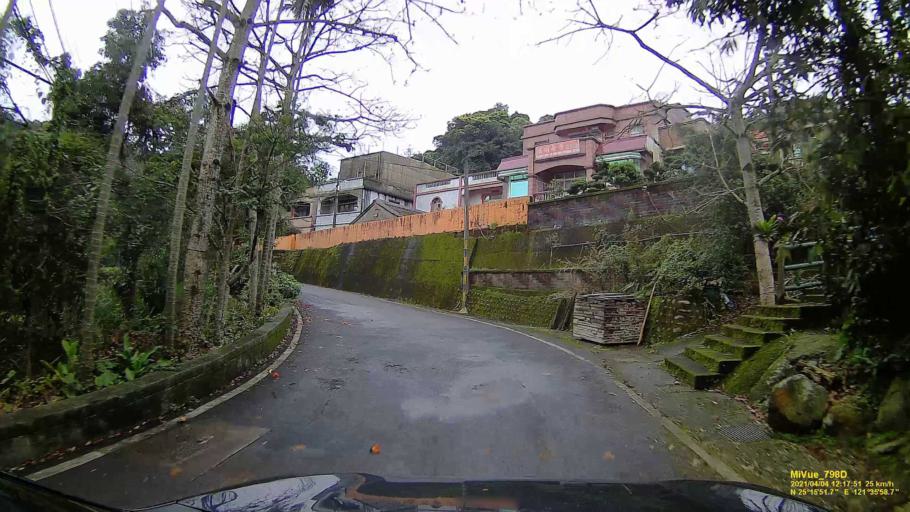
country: TW
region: Taiwan
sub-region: Keelung
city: Keelung
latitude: 25.2643
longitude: 121.5998
